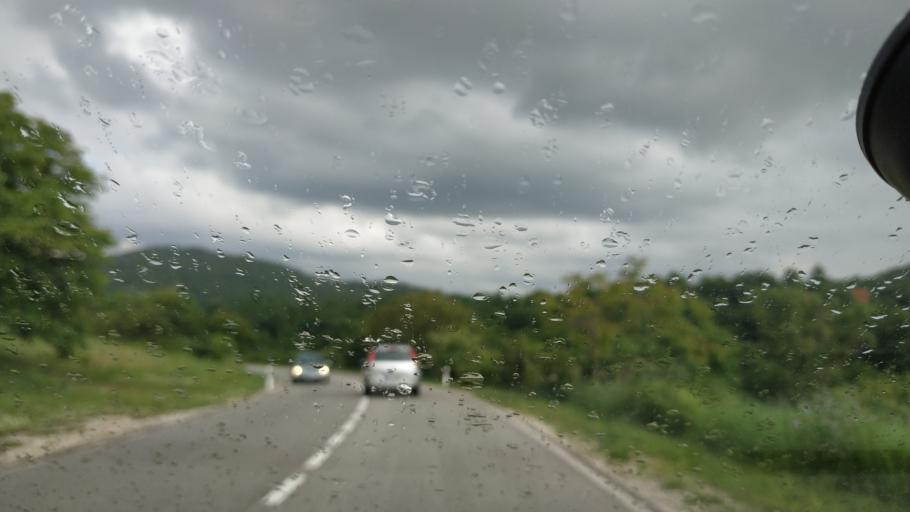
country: RS
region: Central Serbia
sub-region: Borski Okrug
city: Bor
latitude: 44.0587
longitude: 22.0530
